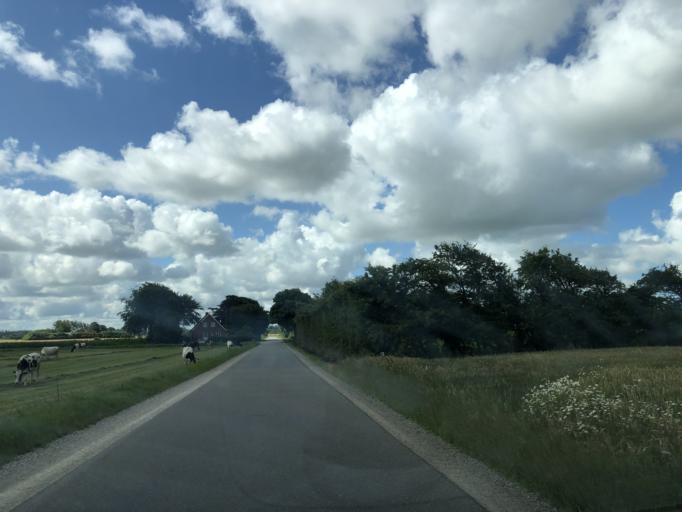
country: DK
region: Central Jutland
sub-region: Struer Kommune
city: Struer
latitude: 56.4469
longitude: 8.5188
